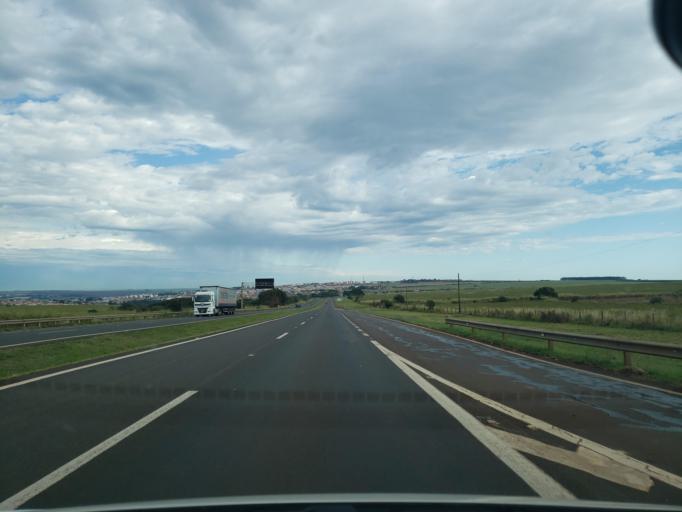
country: BR
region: Sao Paulo
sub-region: Jau
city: Jau
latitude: -22.2653
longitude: -48.5169
